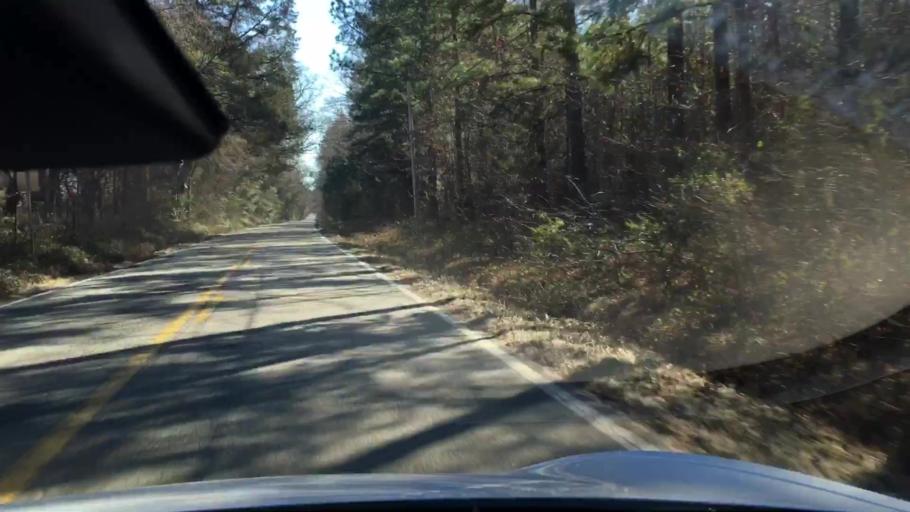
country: US
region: Virginia
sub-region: Henrico County
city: Short Pump
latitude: 37.5842
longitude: -77.7467
